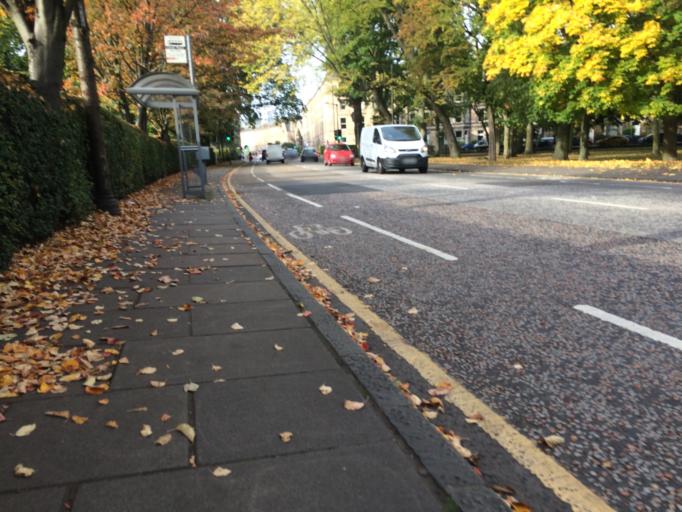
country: GB
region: Scotland
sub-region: Edinburgh
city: Edinburgh
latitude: 55.9412
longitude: -3.1998
